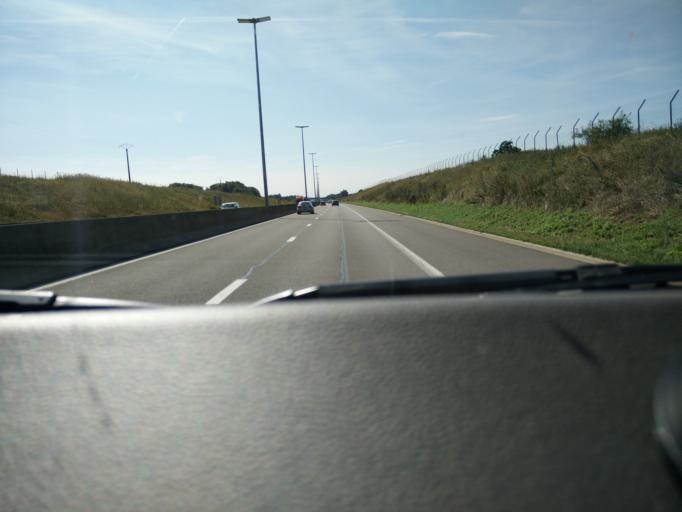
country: BE
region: Wallonia
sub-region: Province du Luxembourg
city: Leglise
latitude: 49.8415
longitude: 5.5108
